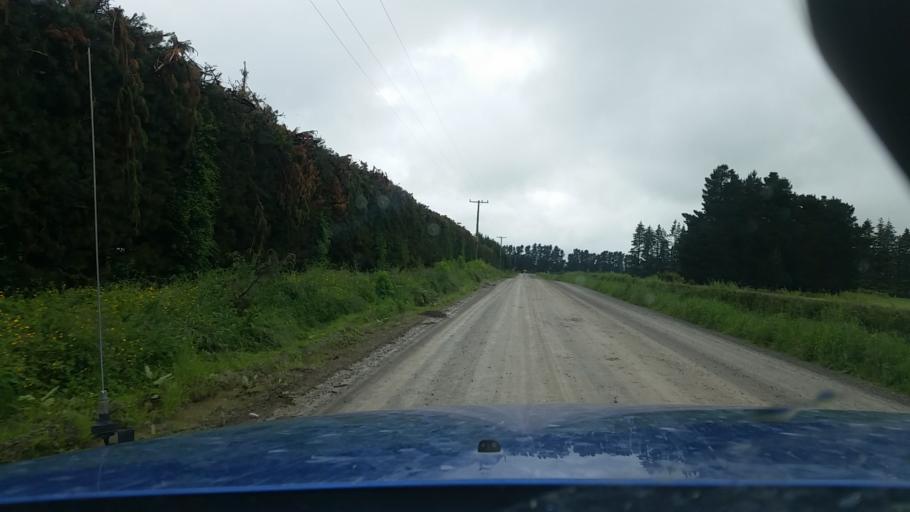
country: NZ
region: Canterbury
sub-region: Ashburton District
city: Methven
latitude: -43.6134
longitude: 171.4878
